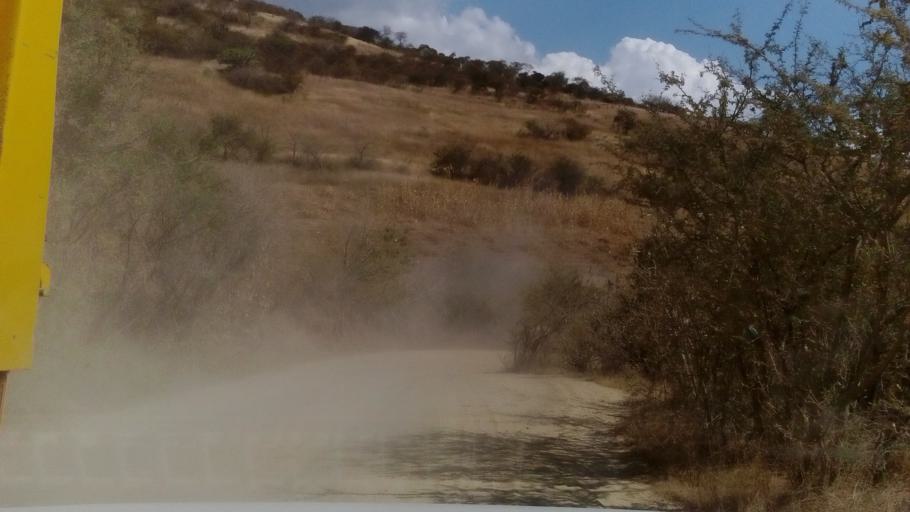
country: MX
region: Guanajuato
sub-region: Silao de la Victoria
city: Loma de Yerbabuena
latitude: 21.0710
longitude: -101.4566
